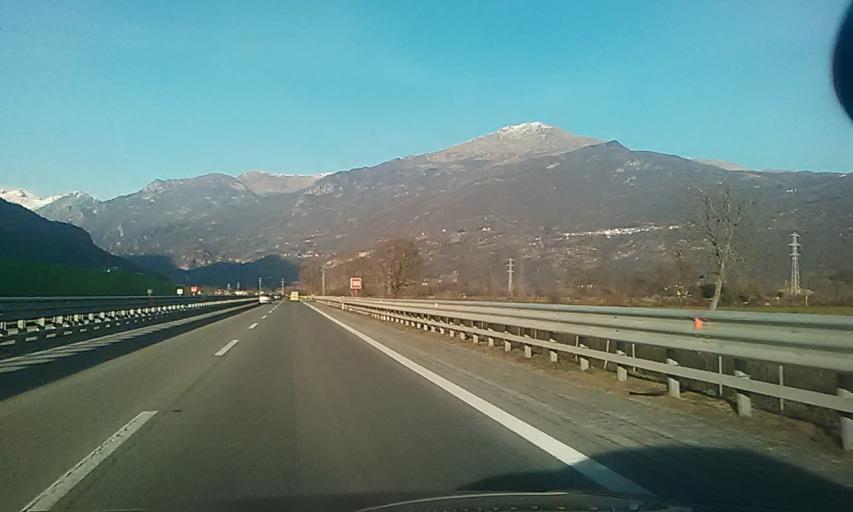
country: IT
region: Piedmont
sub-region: Provincia di Torino
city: Quassolo
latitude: 45.5093
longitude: 7.8329
